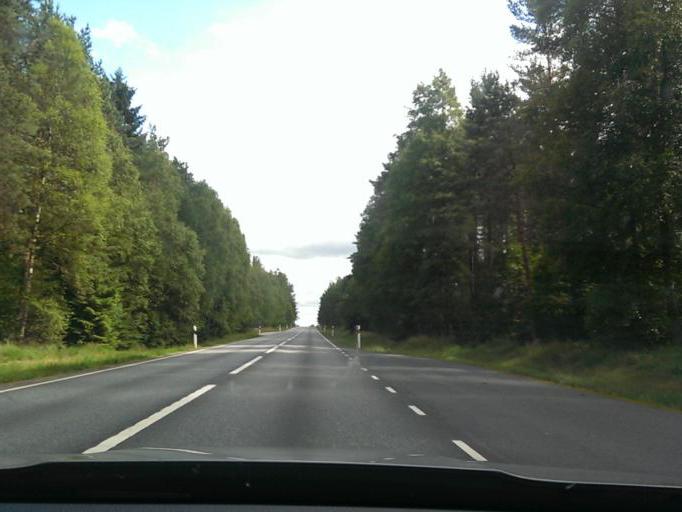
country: SE
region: Joenkoeping
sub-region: Varnamo Kommun
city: Varnamo
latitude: 57.2452
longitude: 13.9936
